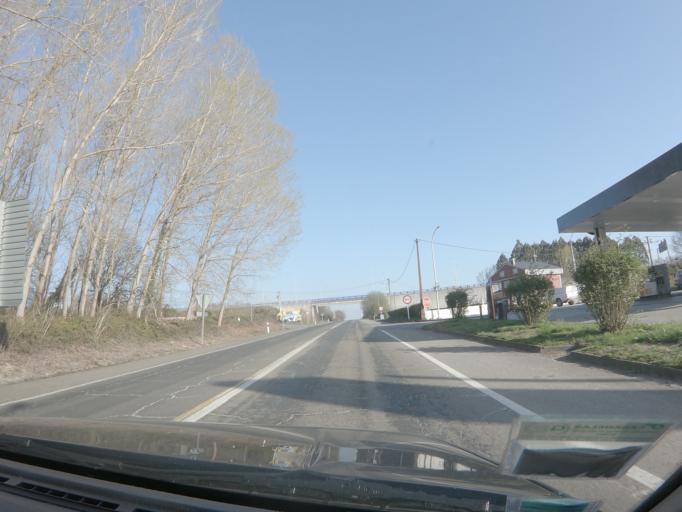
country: ES
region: Galicia
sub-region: Provincia de Lugo
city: Corgo
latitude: 42.9673
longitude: -7.4987
